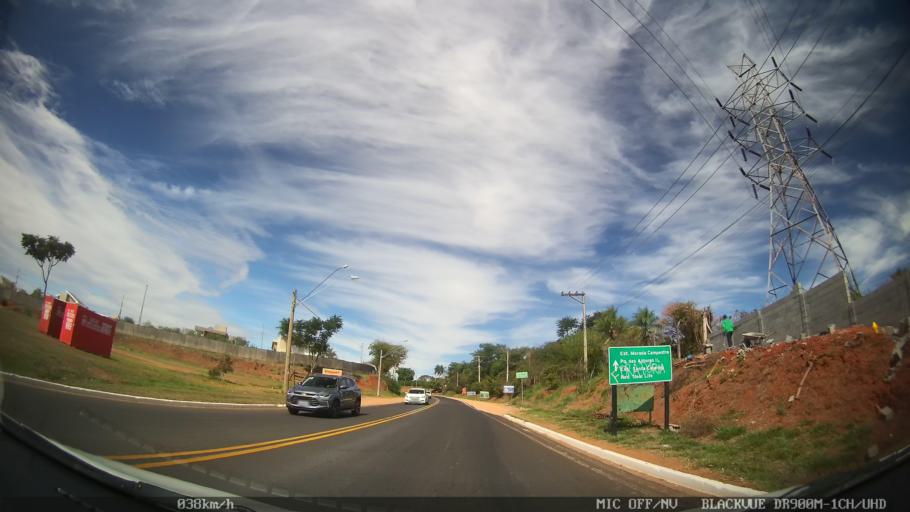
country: BR
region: Sao Paulo
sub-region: Sao Jose Do Rio Preto
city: Sao Jose do Rio Preto
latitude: -20.8285
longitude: -49.3430
